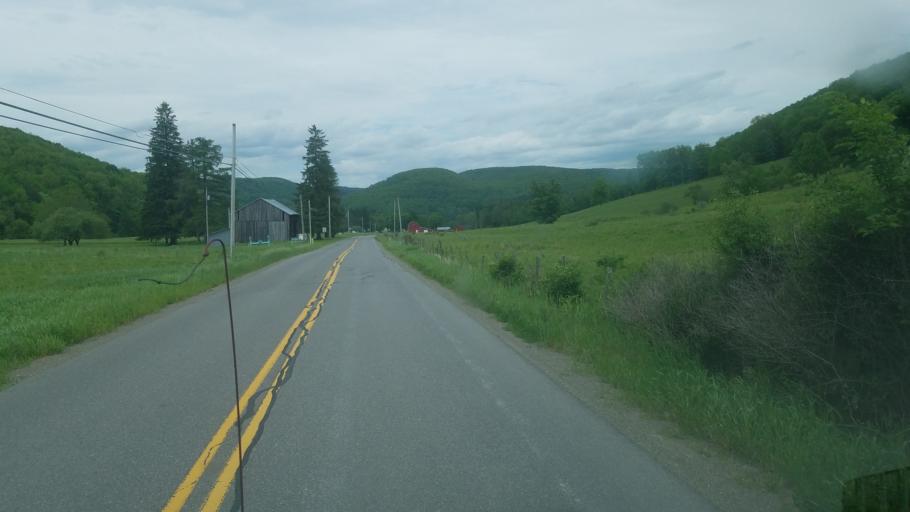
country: US
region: Pennsylvania
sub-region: Tioga County
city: Westfield
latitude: 41.8984
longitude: -77.6052
